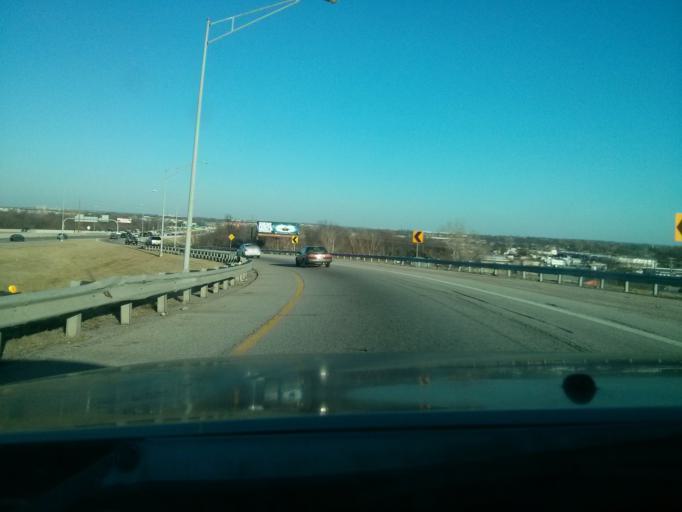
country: US
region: Oklahoma
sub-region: Tulsa County
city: Owasso
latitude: 36.1615
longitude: -95.8804
